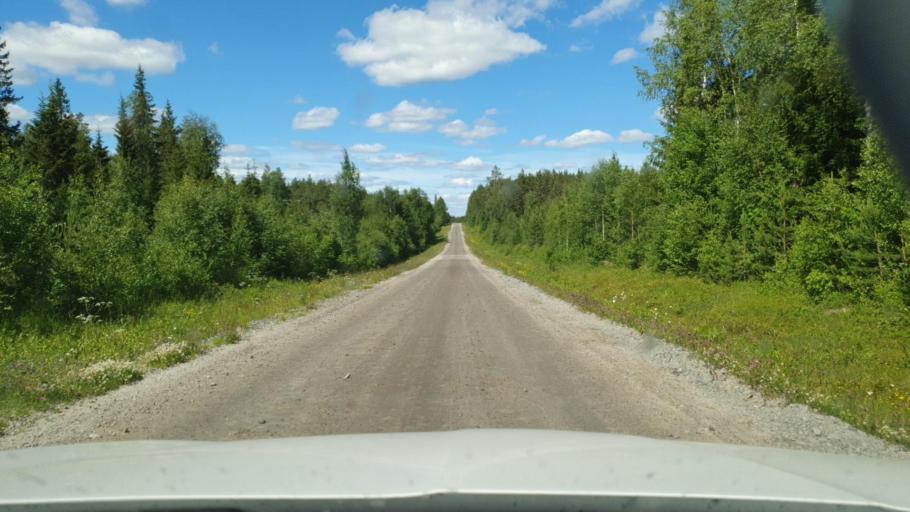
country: SE
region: Vaesterbotten
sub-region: Skelleftea Kommun
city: Byske
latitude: 65.1420
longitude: 21.1771
